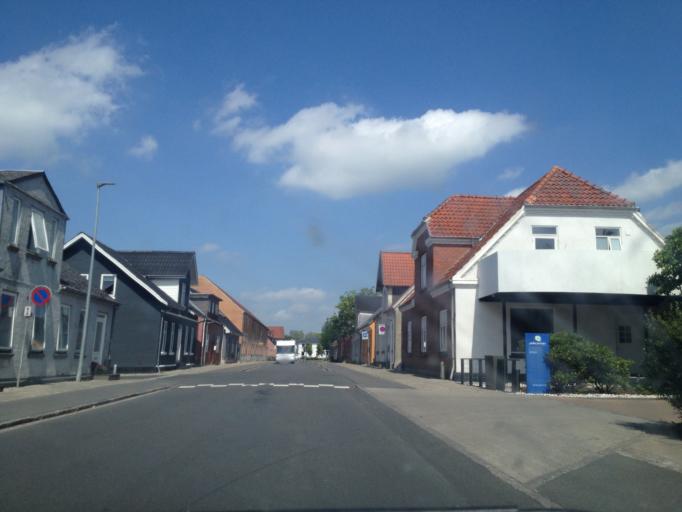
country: DK
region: South Denmark
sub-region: Kolding Kommune
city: Vamdrup
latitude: 55.4245
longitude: 9.2802
